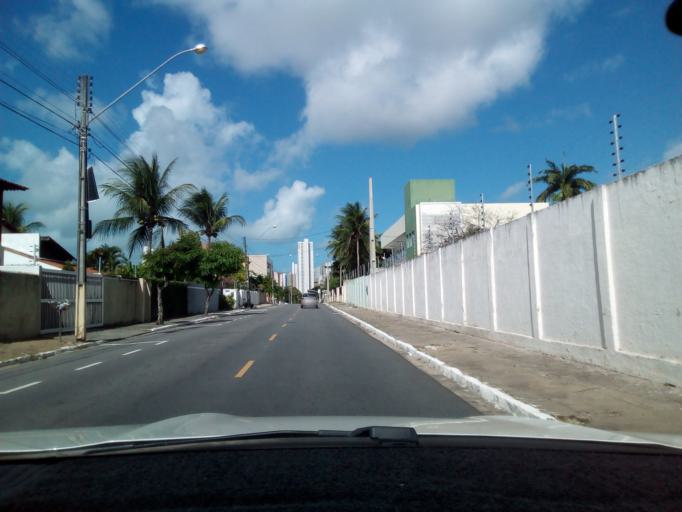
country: BR
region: Paraiba
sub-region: Joao Pessoa
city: Joao Pessoa
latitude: -7.1156
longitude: -34.8514
